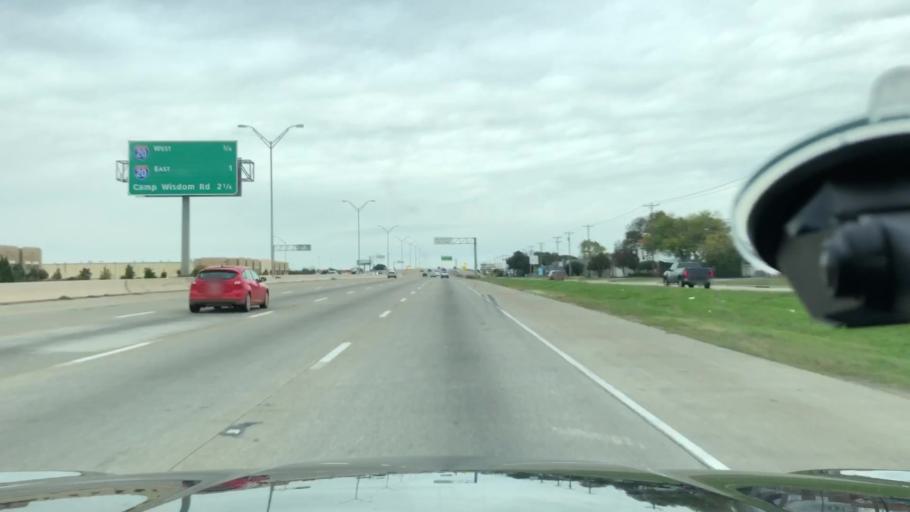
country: US
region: Texas
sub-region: Dallas County
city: DeSoto
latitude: 32.6268
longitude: -96.8230
